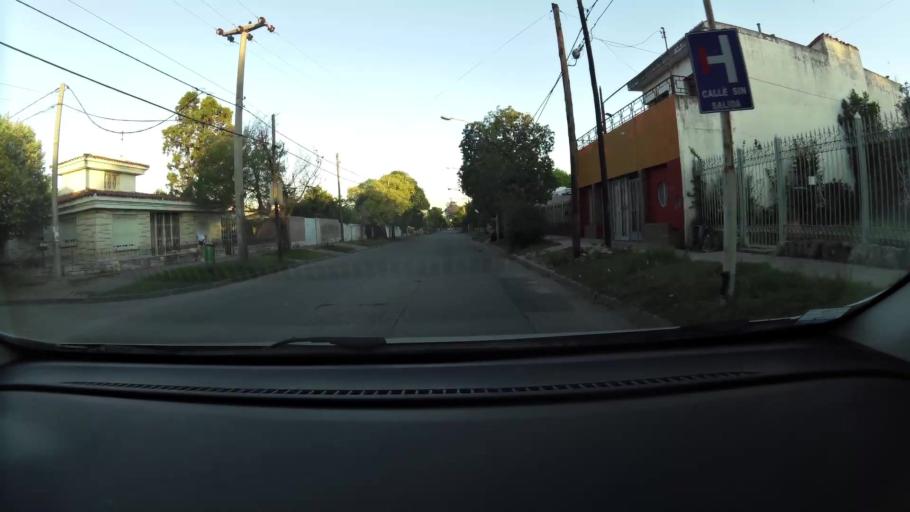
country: AR
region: Cordoba
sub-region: Departamento de Capital
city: Cordoba
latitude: -31.3724
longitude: -64.2206
